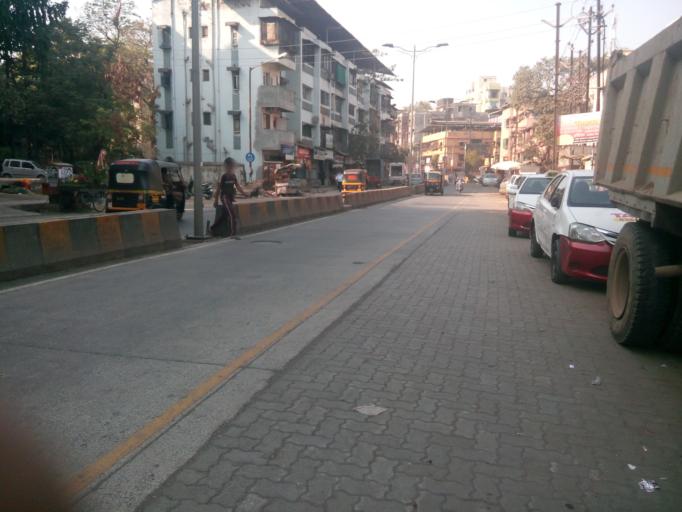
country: IN
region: Maharashtra
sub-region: Thane
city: Dombivli
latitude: 19.2113
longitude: 73.0928
